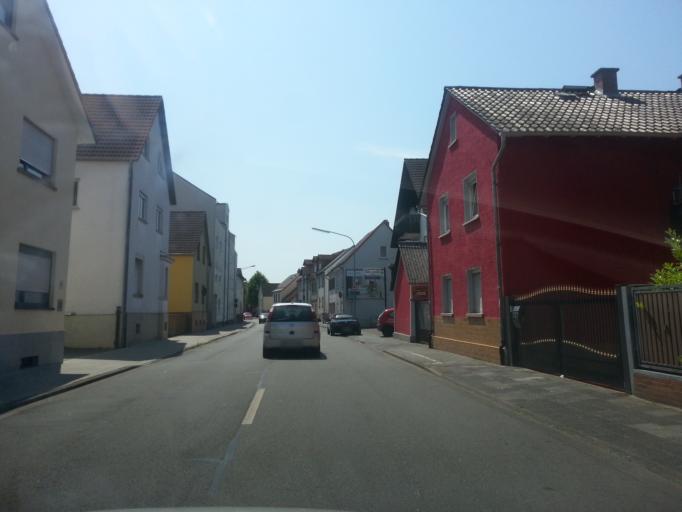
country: DE
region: Hesse
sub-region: Regierungsbezirk Darmstadt
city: Eppertshausen
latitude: 49.9811
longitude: 8.8250
